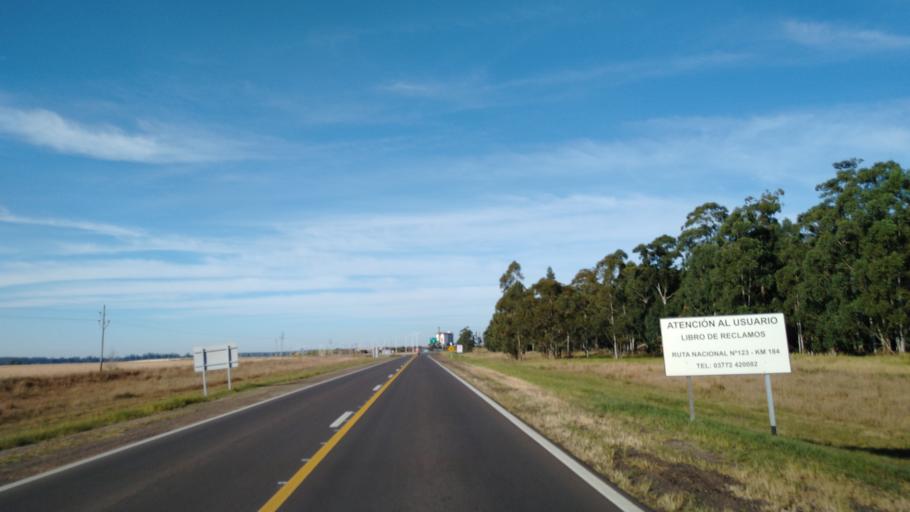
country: AR
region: Corrientes
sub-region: Departamento de Paso de los Libres
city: Paso de los Libres
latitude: -29.7033
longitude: -57.2110
